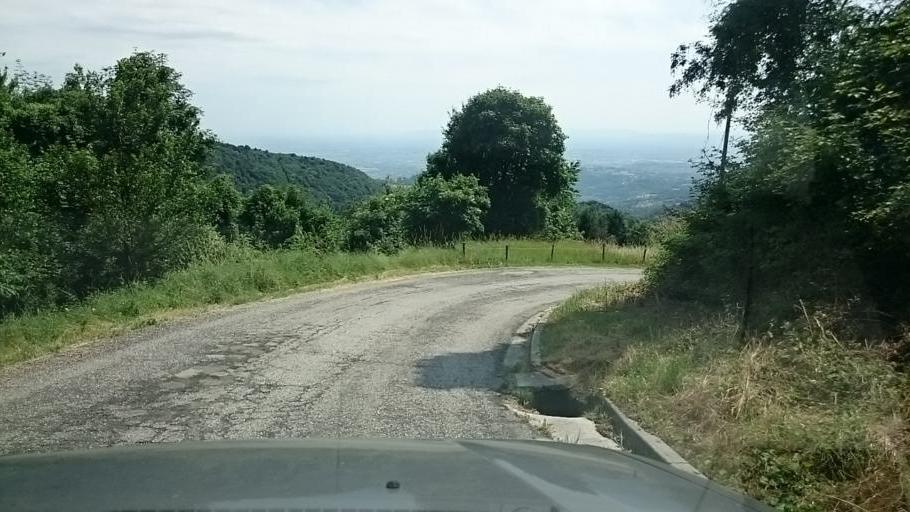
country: IT
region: Veneto
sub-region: Provincia di Vicenza
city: Conco
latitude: 45.7913
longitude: 11.6048
